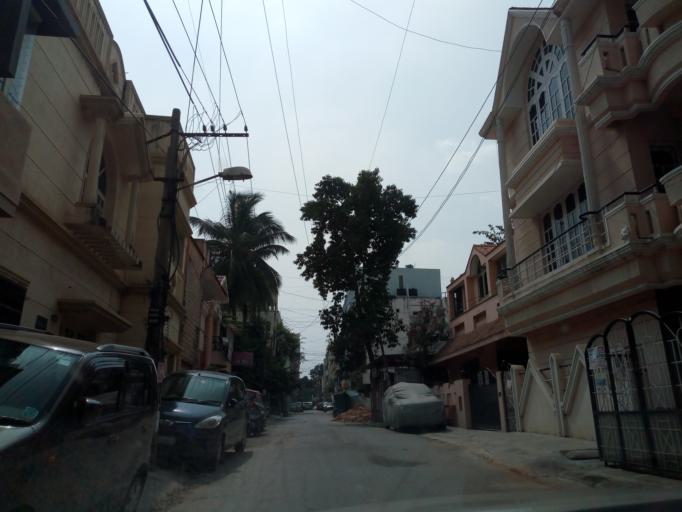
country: IN
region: Karnataka
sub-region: Bangalore Urban
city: Bangalore
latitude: 12.9185
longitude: 77.6074
